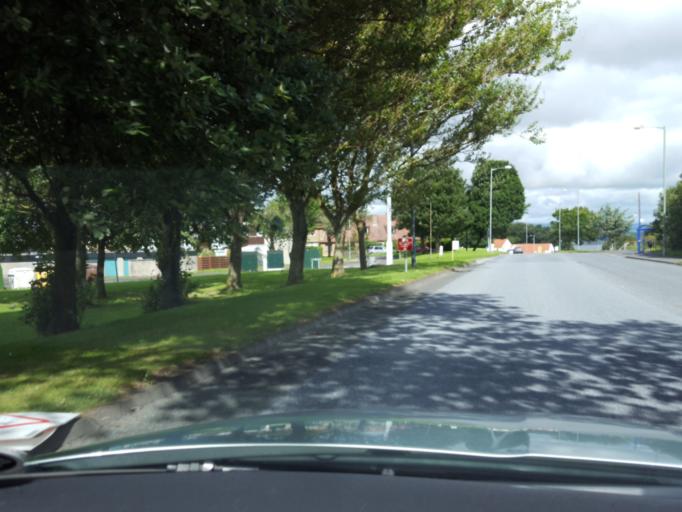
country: GB
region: Scotland
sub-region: Falkirk
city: Bo'ness
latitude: 56.0105
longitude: -3.5881
